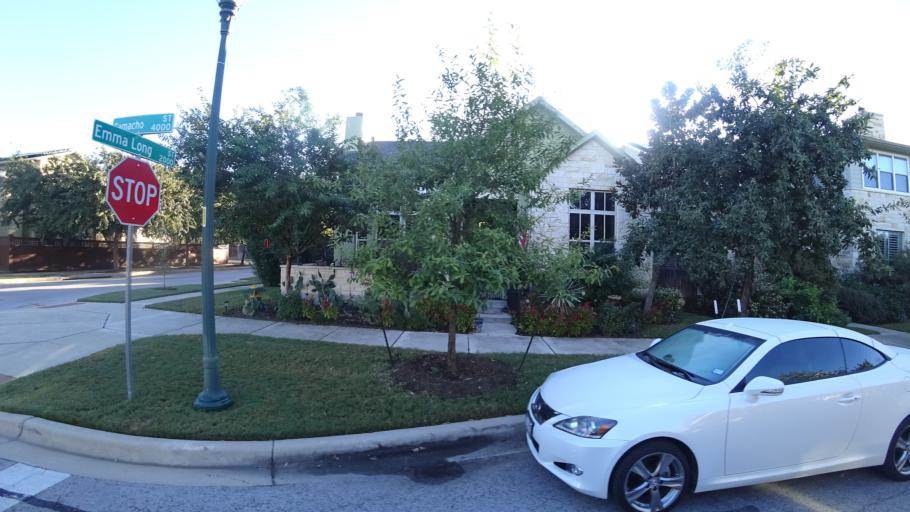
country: US
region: Texas
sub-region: Travis County
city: Austin
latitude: 30.2919
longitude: -97.7051
